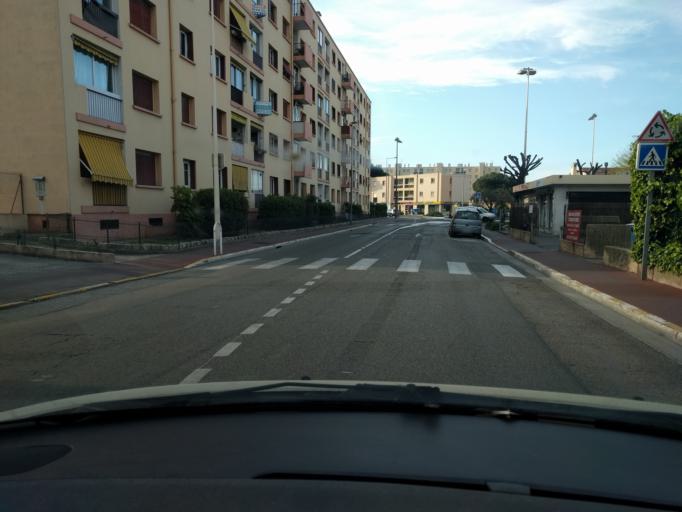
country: FR
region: Provence-Alpes-Cote d'Azur
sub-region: Departement des Alpes-Maritimes
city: Cannes
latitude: 43.5548
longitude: 6.9731
